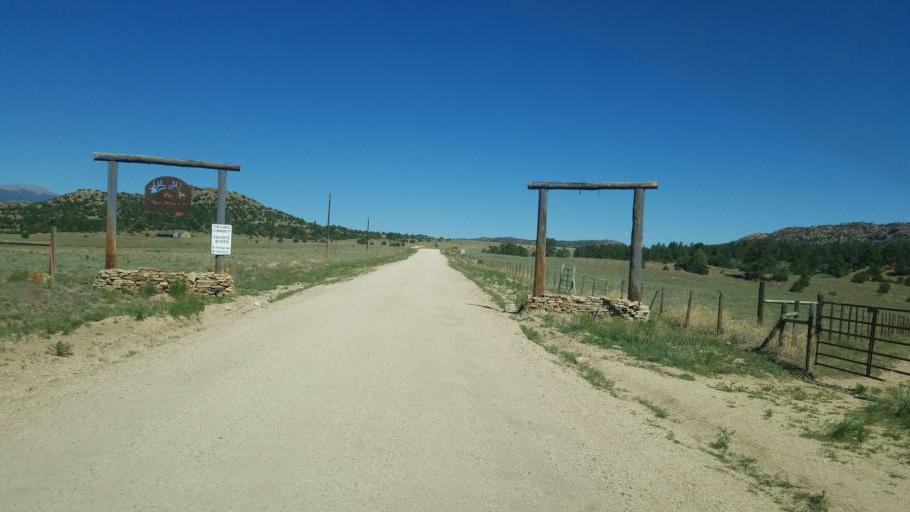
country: US
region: Colorado
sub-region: Custer County
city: Westcliffe
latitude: 38.2168
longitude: -105.4497
